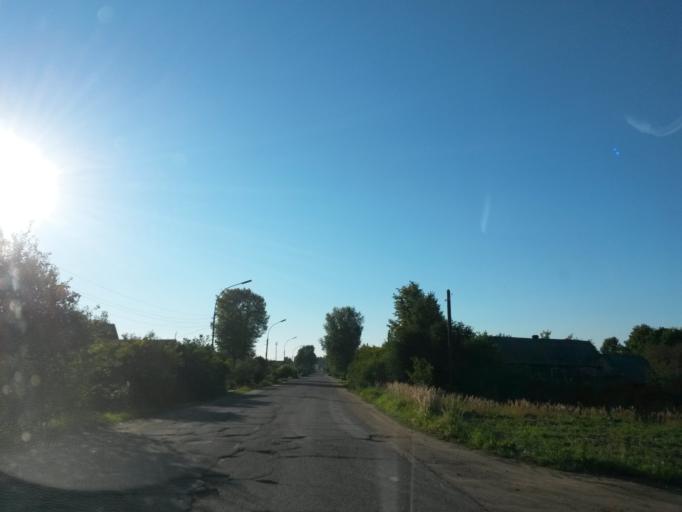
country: RU
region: Jaroslavl
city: Gavrilov-Yam
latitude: 57.2957
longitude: 39.8751
